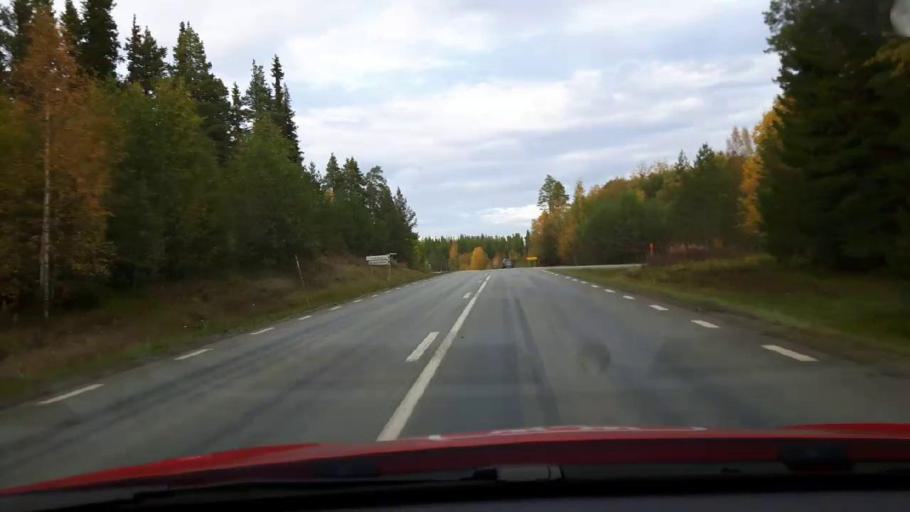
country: SE
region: Jaemtland
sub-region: Krokoms Kommun
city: Krokom
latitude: 63.3398
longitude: 14.4653
